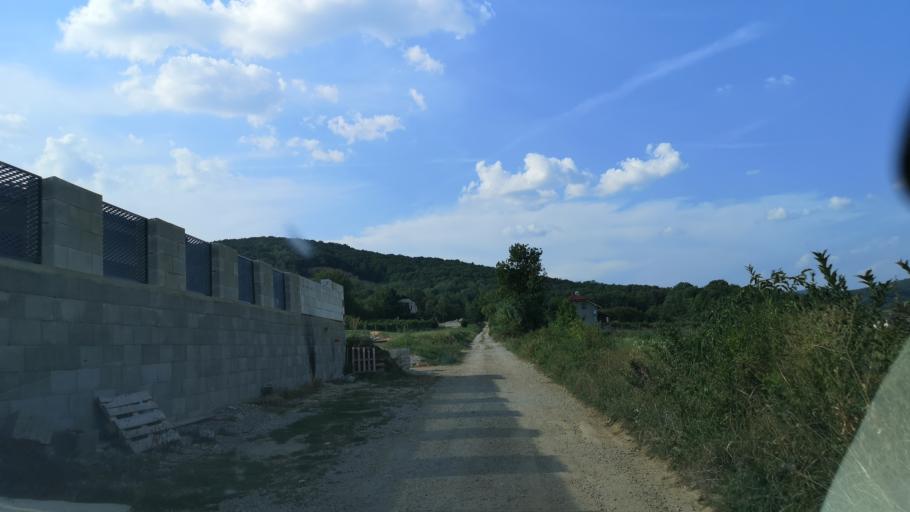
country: SK
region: Nitriansky
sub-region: Okres Nitra
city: Nitra
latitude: 48.3806
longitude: 18.2154
